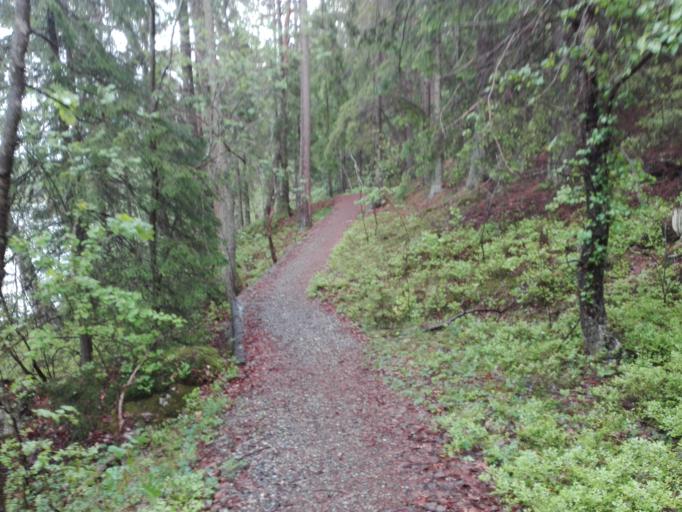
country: SE
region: Stockholm
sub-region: Nacka Kommun
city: Fisksatra
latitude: 59.2952
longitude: 18.2644
